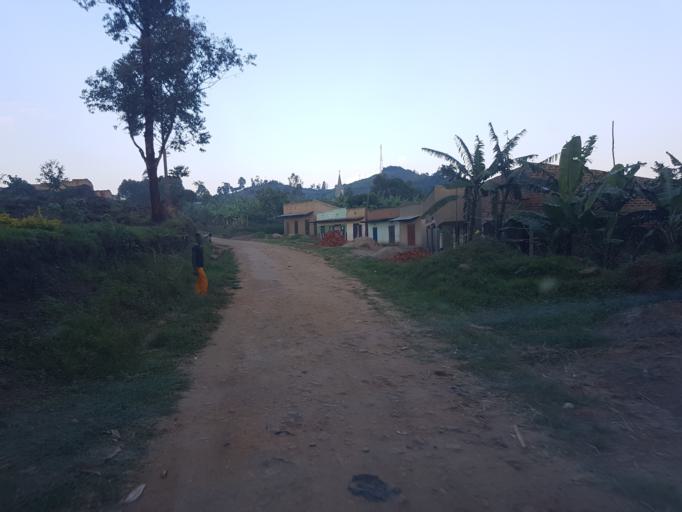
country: UG
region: Western Region
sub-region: Mitoma District
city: Mitoma
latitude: -0.6776
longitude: 29.9257
